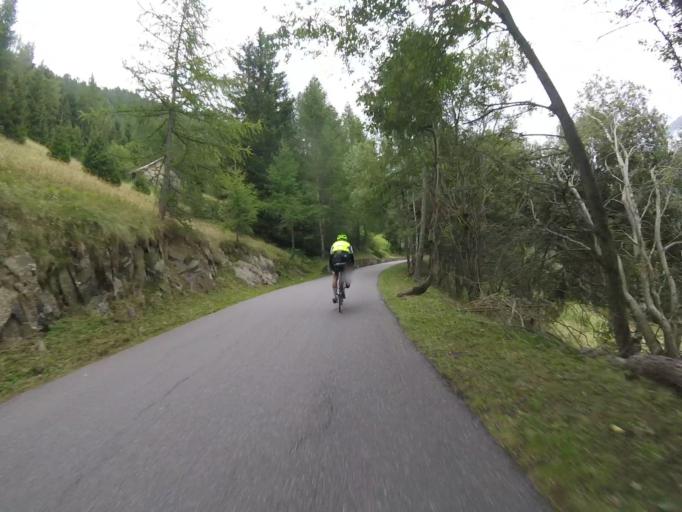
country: IT
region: Lombardy
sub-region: Provincia di Brescia
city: Monno
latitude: 46.2362
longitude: 10.3210
